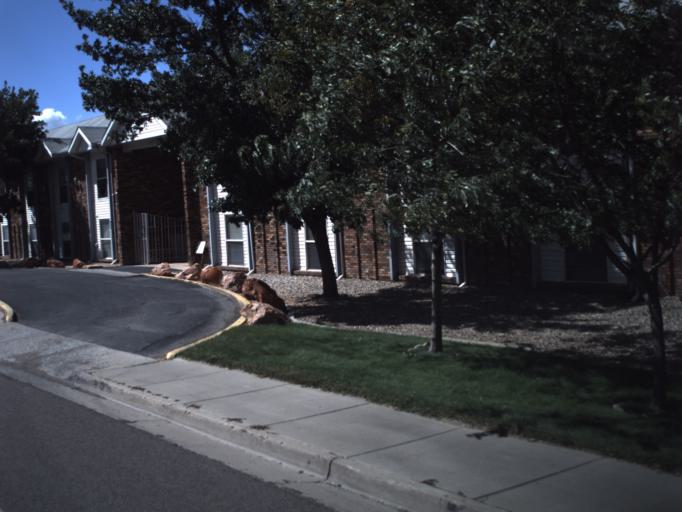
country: US
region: Utah
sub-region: Iron County
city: Cedar City
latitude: 37.6628
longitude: -113.0684
